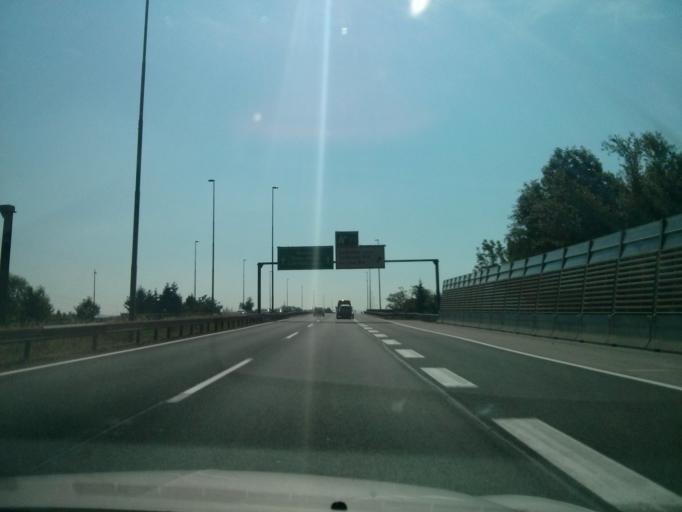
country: SI
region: Brezovica
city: Vnanje Gorice
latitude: 46.0366
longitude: 14.4574
